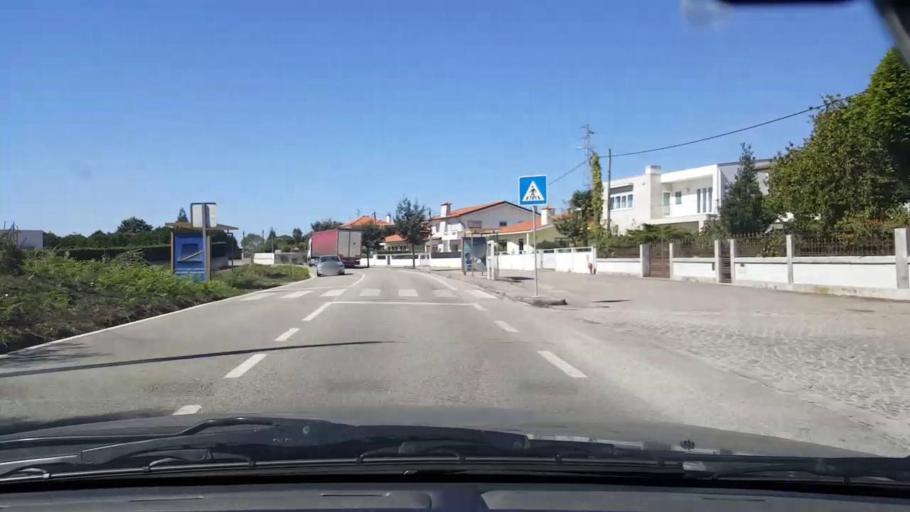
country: PT
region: Porto
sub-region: Vila do Conde
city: Arvore
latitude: 41.3407
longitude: -8.6954
